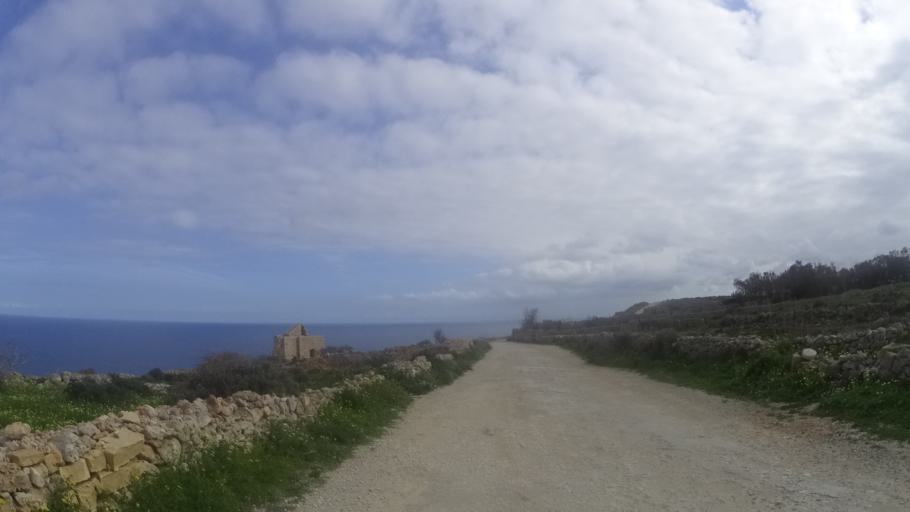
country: MT
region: Il-Qala
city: Qala
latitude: 36.0408
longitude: 14.3206
